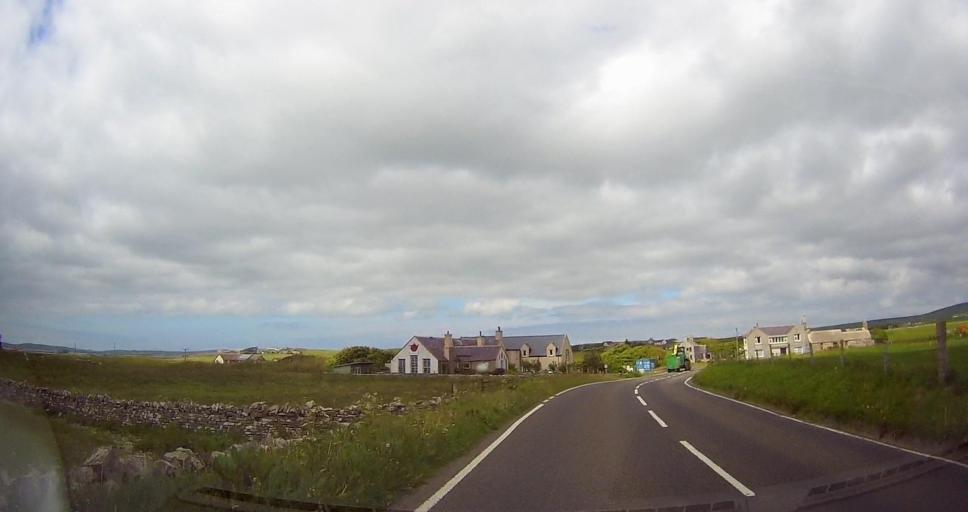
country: GB
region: Scotland
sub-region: Orkney Islands
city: Stromness
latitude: 59.0345
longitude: -3.1860
